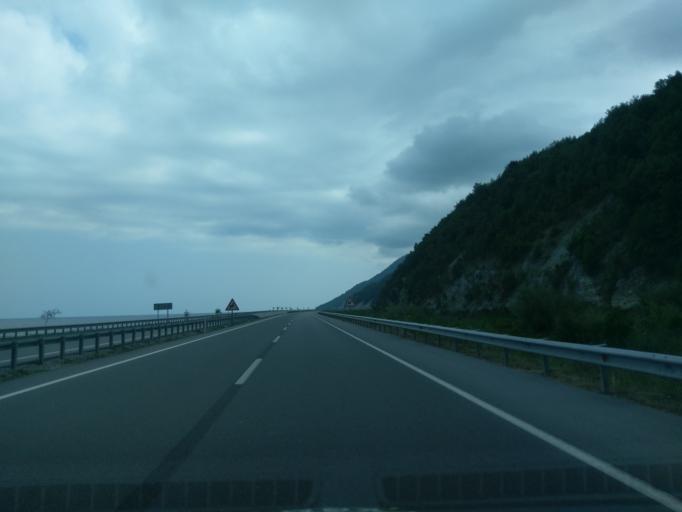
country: TR
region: Sinop
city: Dikmen
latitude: 41.7081
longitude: 35.2995
